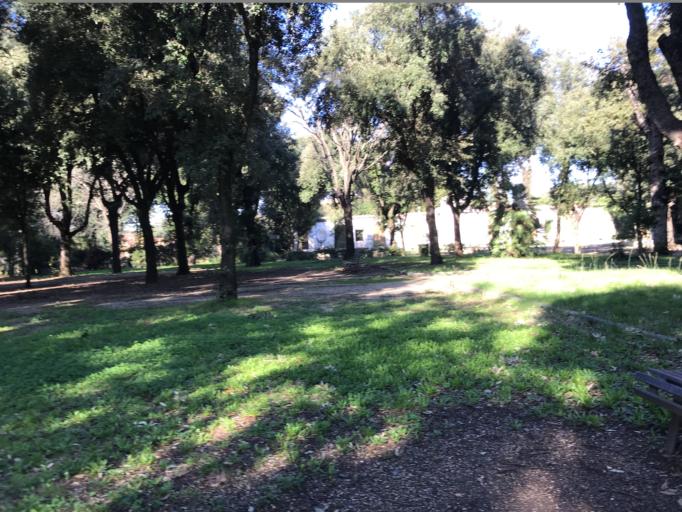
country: IT
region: Latium
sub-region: Citta metropolitana di Roma Capitale
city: Rome
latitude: 41.9159
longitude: 12.4907
